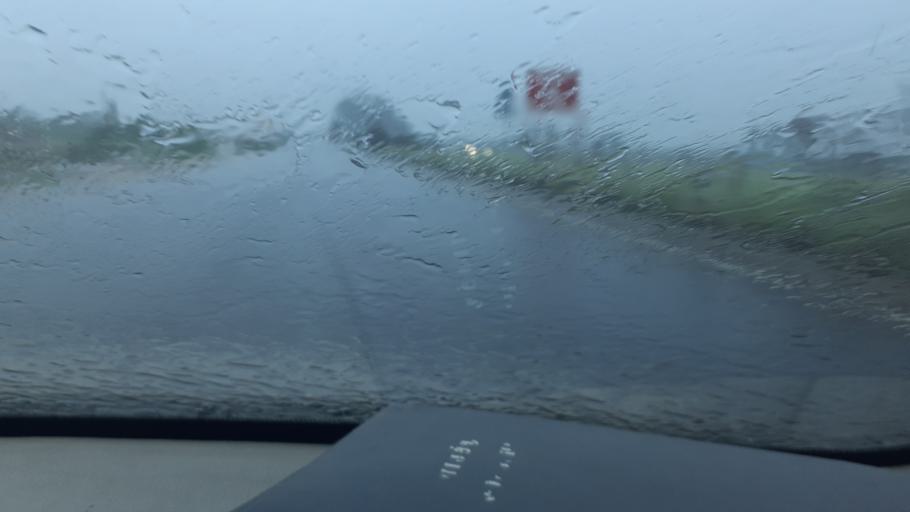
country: IN
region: Tamil Nadu
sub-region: Virudhunagar
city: Sattur
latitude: 9.4404
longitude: 77.9245
